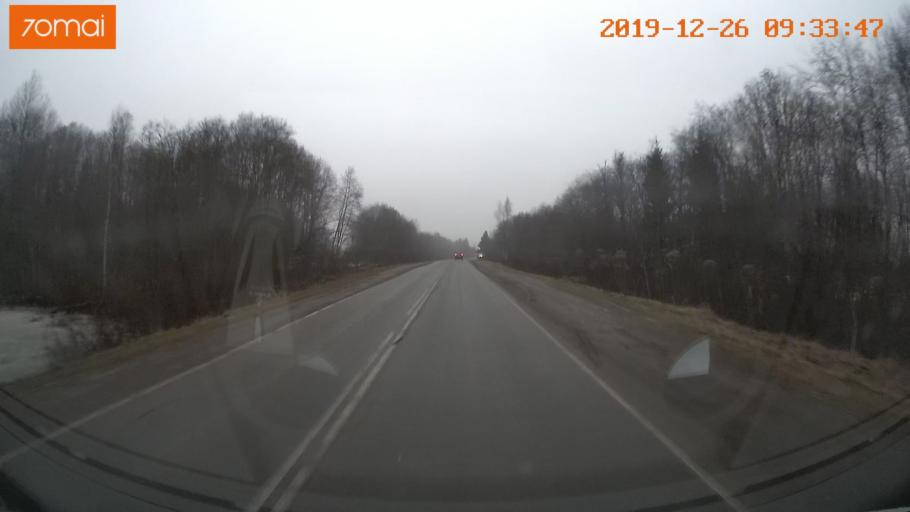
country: RU
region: Vologda
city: Vologda
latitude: 59.0939
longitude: 40.0952
